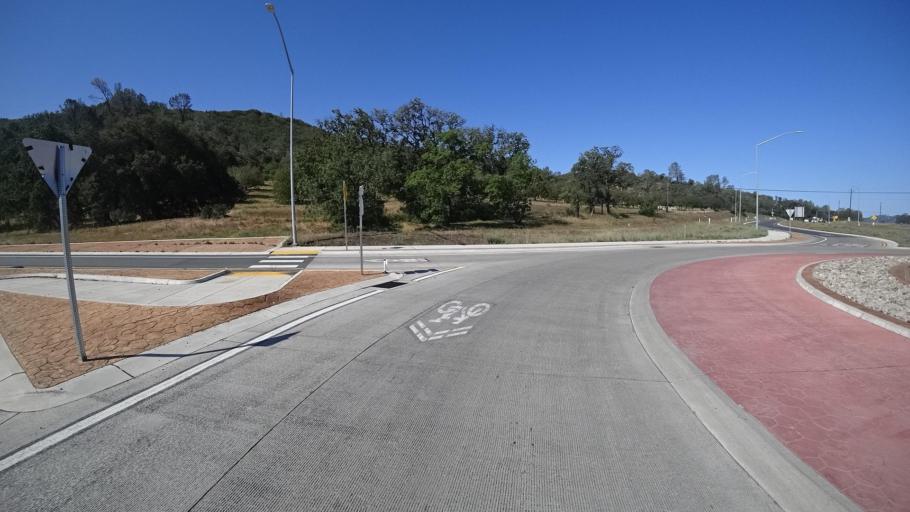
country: US
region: California
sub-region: Lake County
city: Clearlake
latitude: 39.0084
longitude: -122.6142
